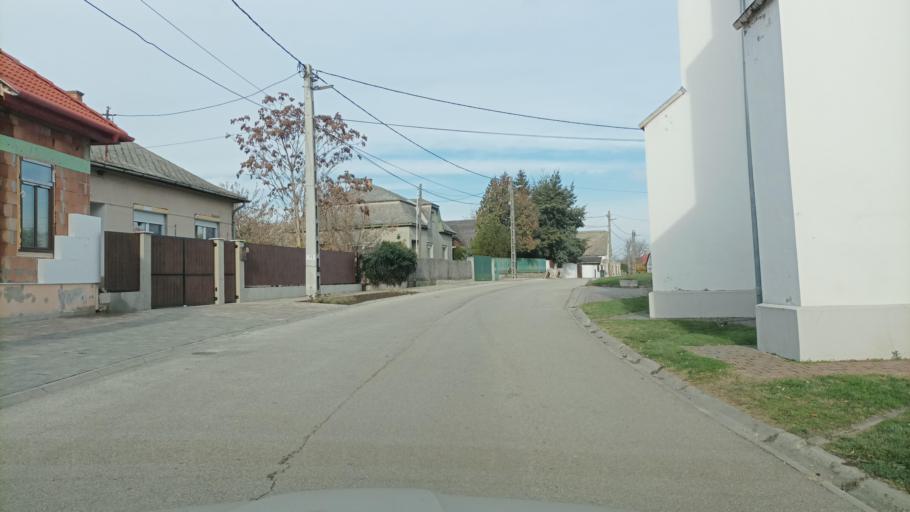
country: HU
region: Fejer
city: Adony
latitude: 47.0897
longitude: 18.9254
